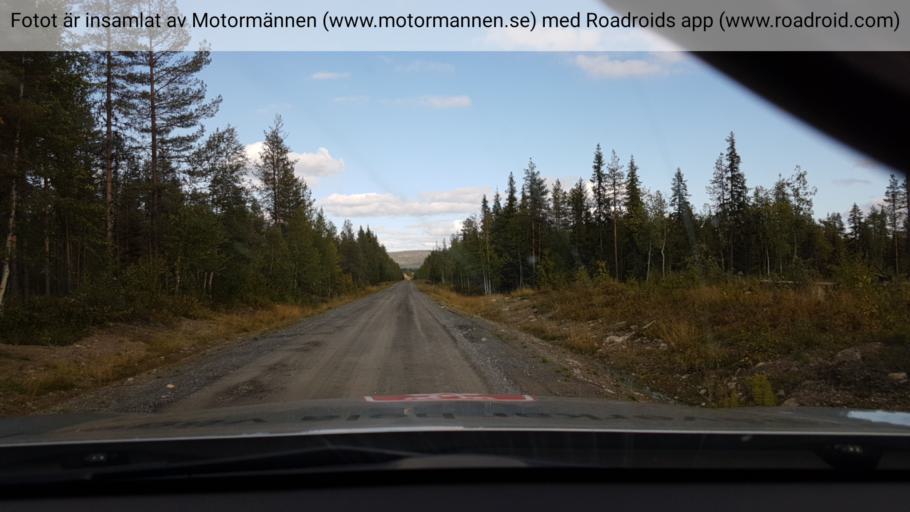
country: SE
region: Vaesterbotten
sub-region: Sorsele Kommun
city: Sorsele
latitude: 65.4582
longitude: 17.7376
